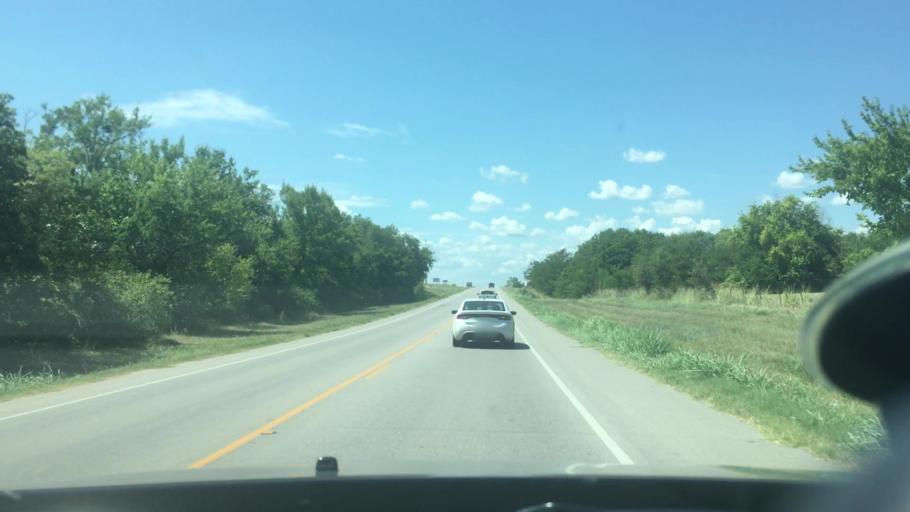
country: US
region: Oklahoma
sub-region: Marshall County
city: Kingston
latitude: 34.0383
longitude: -96.7334
